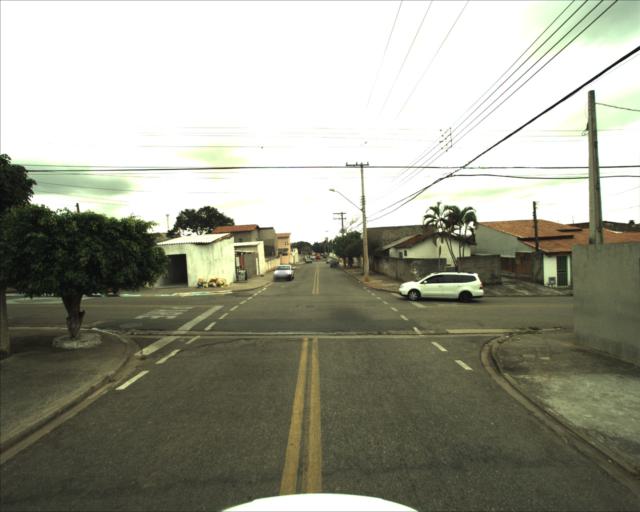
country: BR
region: Sao Paulo
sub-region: Sorocaba
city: Sorocaba
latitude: -23.5061
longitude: -47.5151
